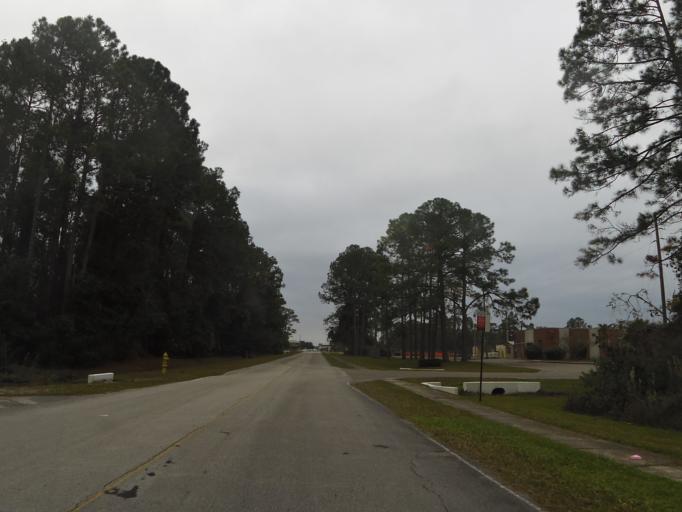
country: US
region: Florida
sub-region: Duval County
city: Baldwin
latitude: 30.2292
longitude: -81.8873
